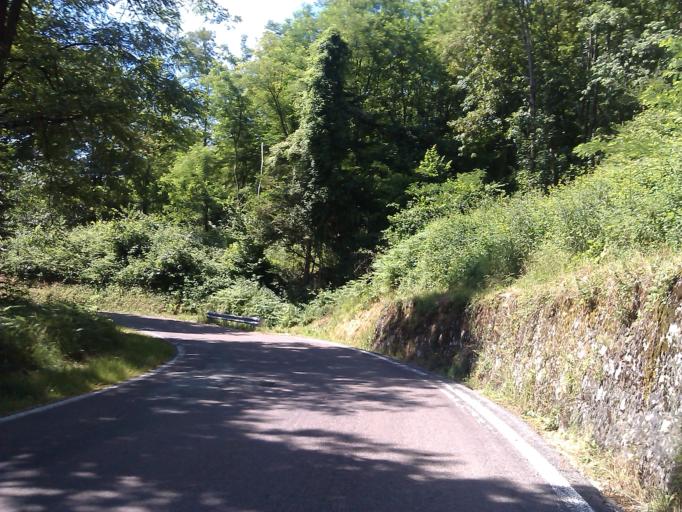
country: IT
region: Tuscany
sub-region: Provincia di Pistoia
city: Sambuca Pistoiese
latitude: 44.1014
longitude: 11.0440
